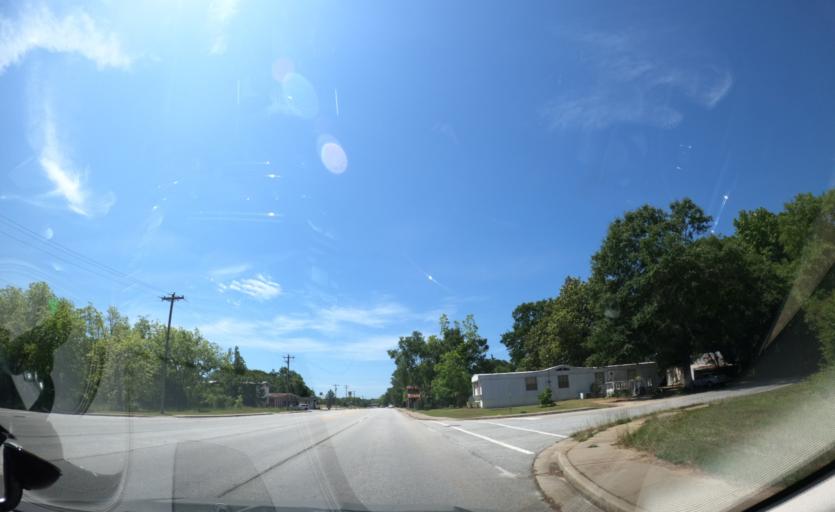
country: US
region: South Carolina
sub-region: Anderson County
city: Iva
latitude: 34.3162
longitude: -82.6634
